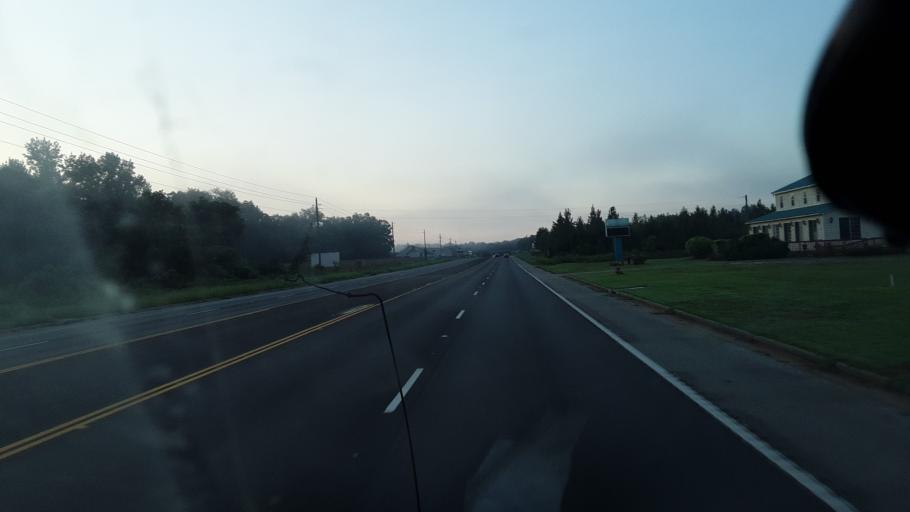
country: US
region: South Carolina
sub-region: Clarendon County
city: Manning
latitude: 33.7460
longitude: -80.2160
